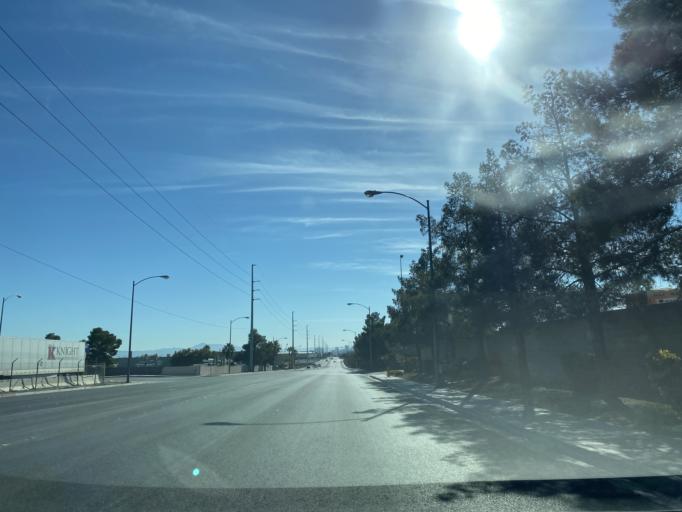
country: US
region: Nevada
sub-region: Clark County
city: North Las Vegas
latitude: 36.2238
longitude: -115.1433
